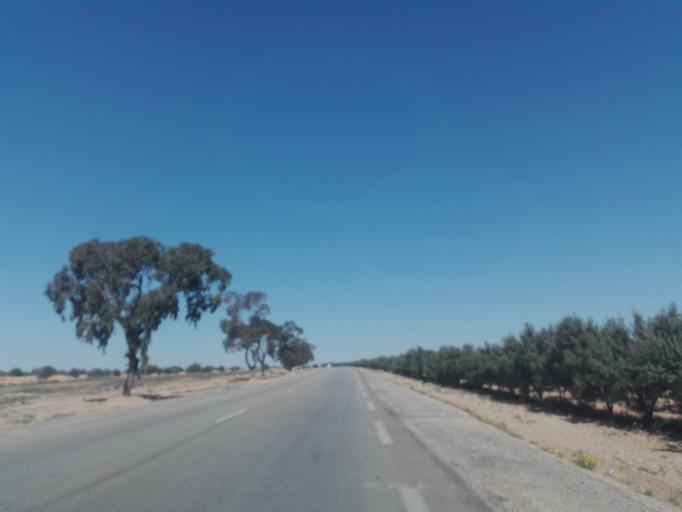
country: TN
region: Safaqis
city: Bi'r `Ali Bin Khalifah
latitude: 34.7497
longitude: 10.3492
